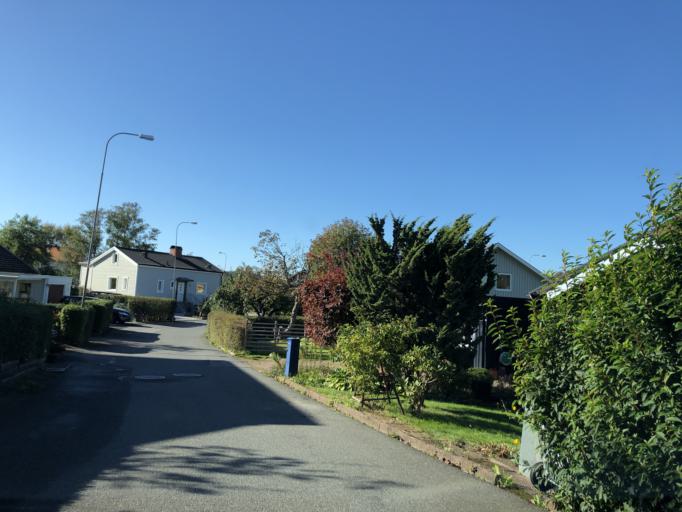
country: SE
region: Vaestra Goetaland
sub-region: Goteborg
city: Majorna
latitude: 57.6626
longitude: 11.8847
